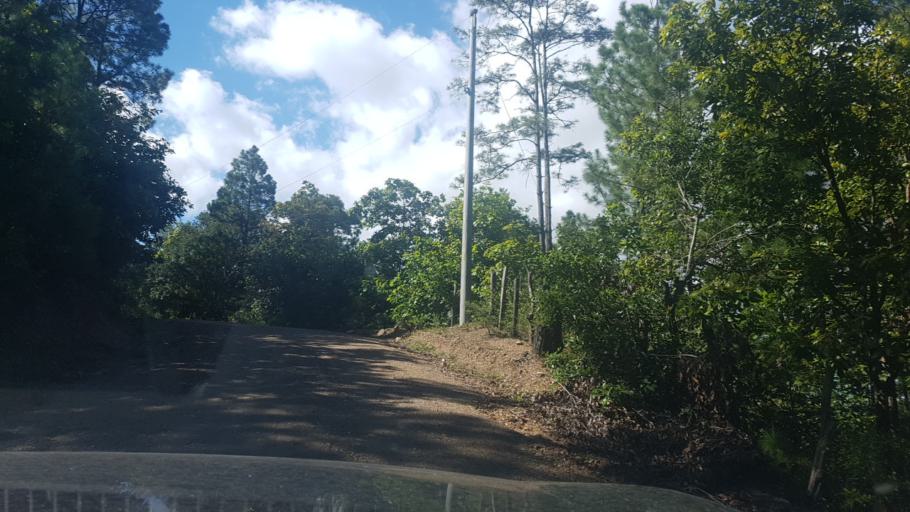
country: NI
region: Nueva Segovia
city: Ocotal
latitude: 13.6418
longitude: -86.6350
